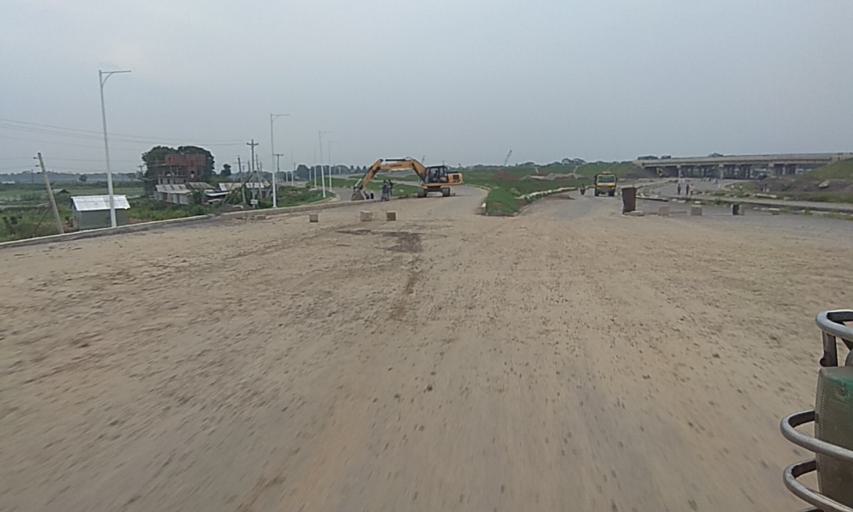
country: BD
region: Dhaka
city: Faridpur
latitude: 23.3927
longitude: 89.9826
